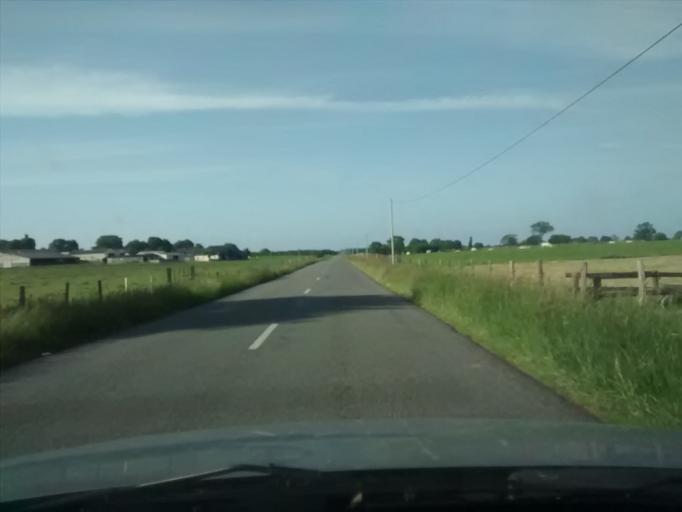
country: FR
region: Pays de la Loire
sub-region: Departement de la Mayenne
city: Meslay-du-Maine
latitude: 47.9598
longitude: -0.6224
